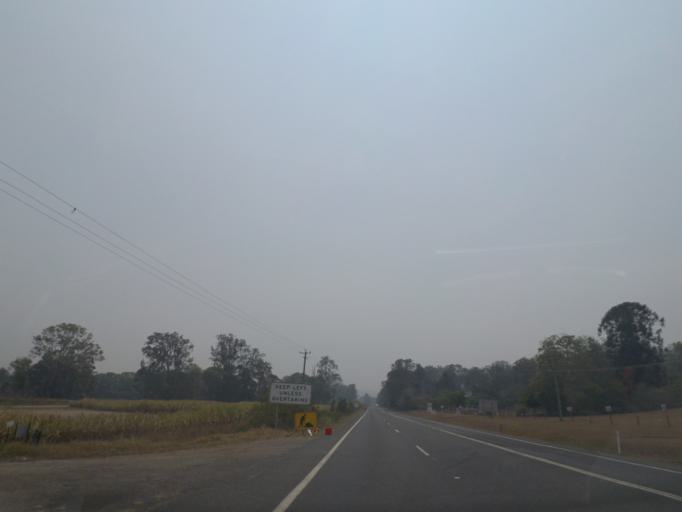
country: AU
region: New South Wales
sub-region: Clarence Valley
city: Maclean
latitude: -29.5604
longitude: 153.1493
